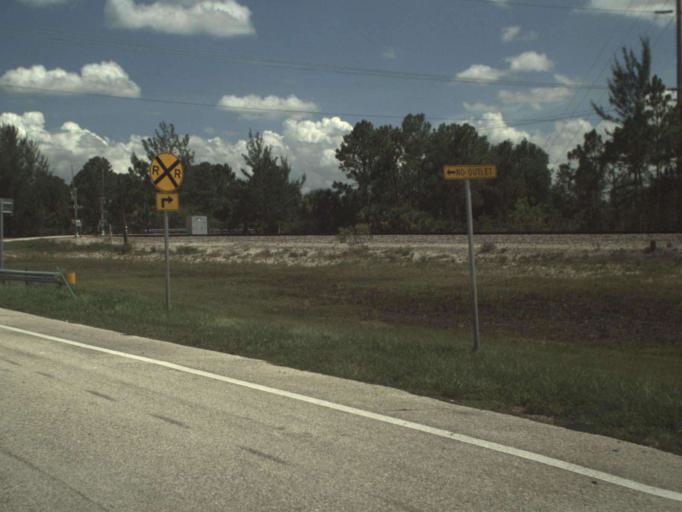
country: US
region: Florida
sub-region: Palm Beach County
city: Palm Beach Gardens
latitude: 26.8642
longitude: -80.2338
